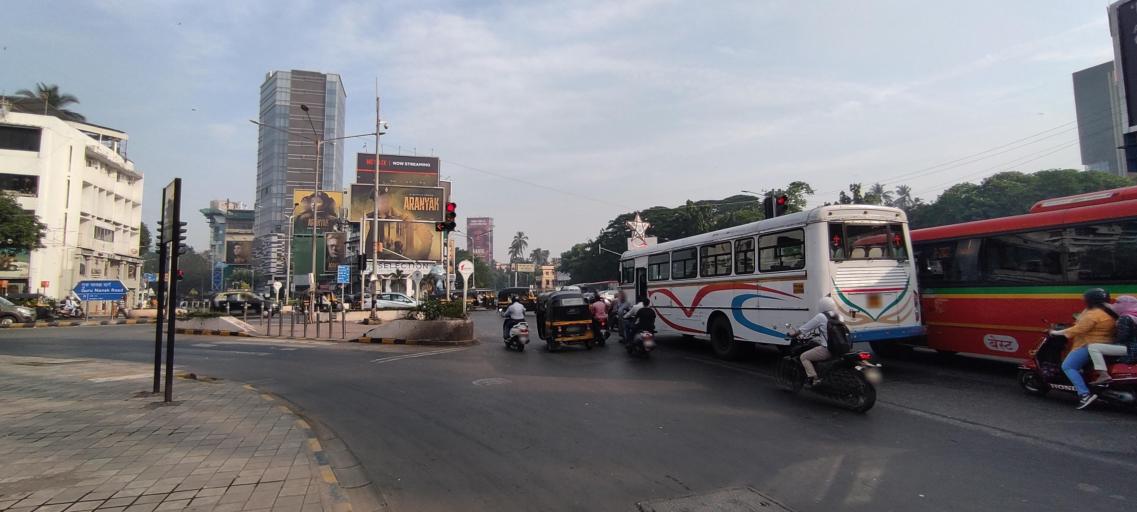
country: IN
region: Maharashtra
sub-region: Mumbai Suburban
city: Mumbai
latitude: 19.0592
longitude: 72.8367
